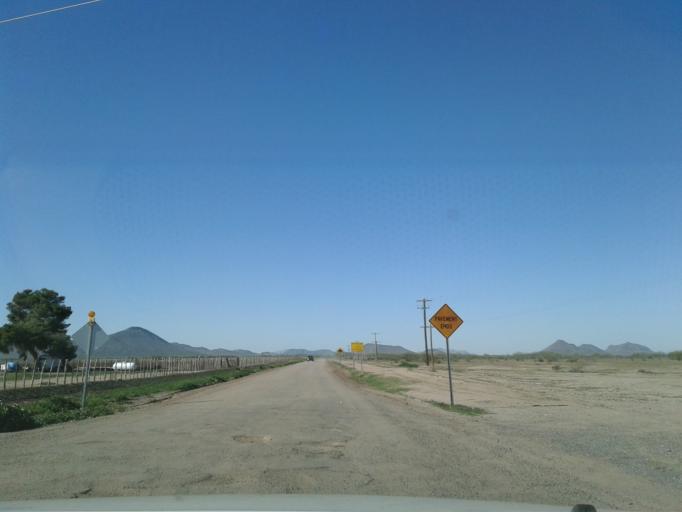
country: US
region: Arizona
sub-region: Pima County
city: Avra Valley
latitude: 32.5543
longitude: -111.3808
